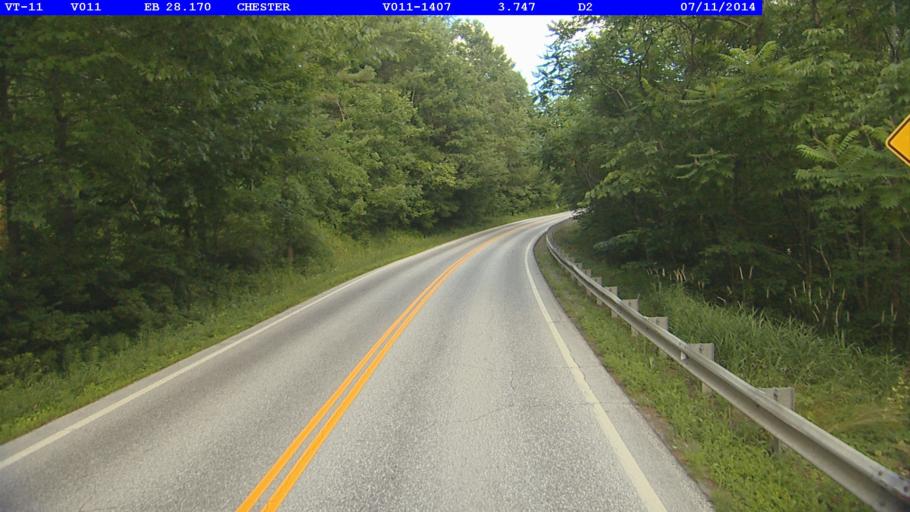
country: US
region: Vermont
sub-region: Windsor County
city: Chester
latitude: 43.2694
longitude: -72.6199
